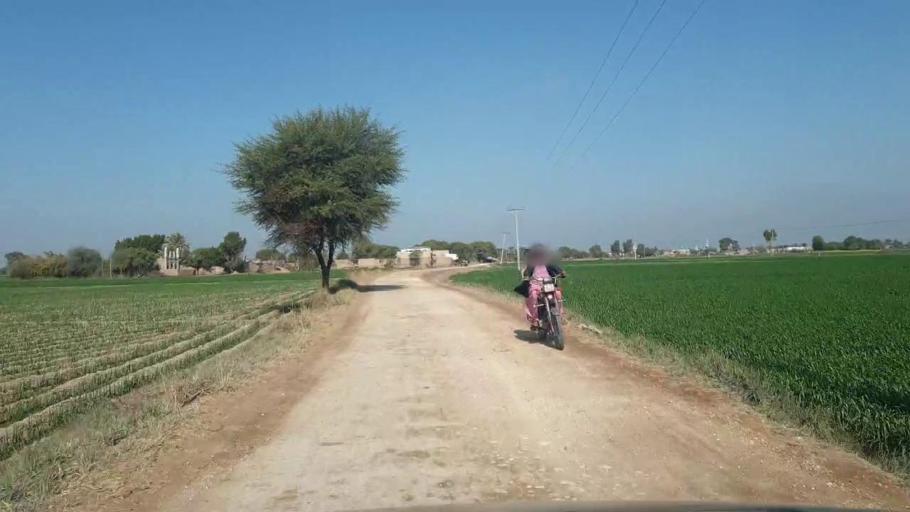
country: PK
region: Sindh
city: Bhit Shah
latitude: 25.8879
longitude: 68.5267
